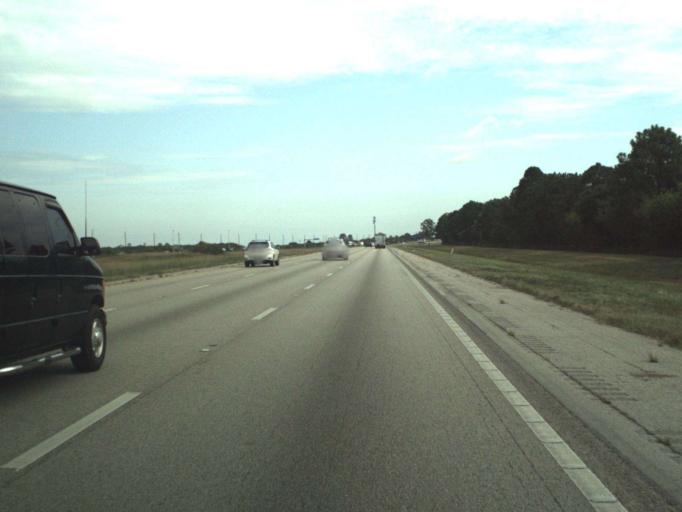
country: US
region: Florida
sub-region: Saint Lucie County
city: Port Saint Lucie
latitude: 27.1915
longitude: -80.3990
